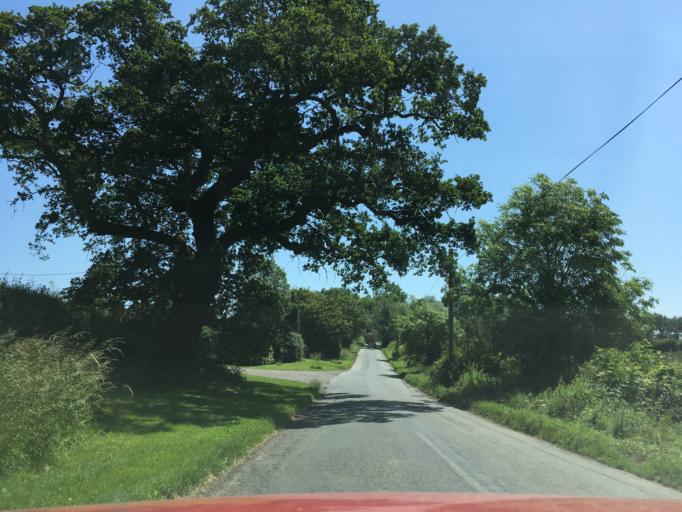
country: GB
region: England
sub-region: Northamptonshire
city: Deanshanger
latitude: 52.0092
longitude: -0.8964
